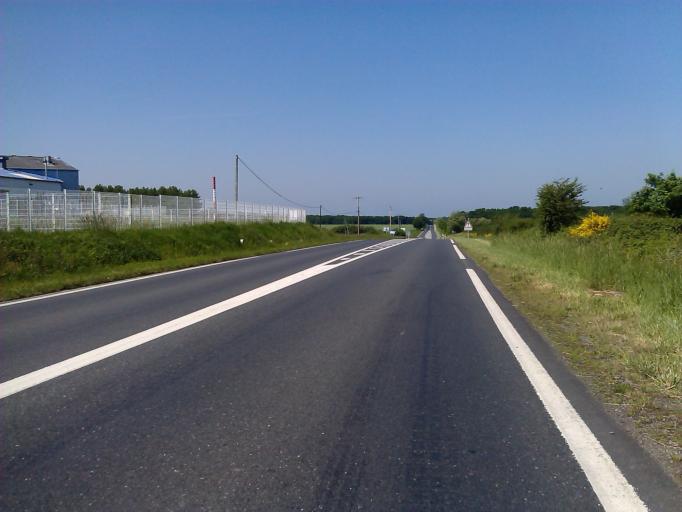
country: FR
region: Centre
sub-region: Departement de l'Indre
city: Le Pechereau
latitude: 46.5990
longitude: 1.5996
